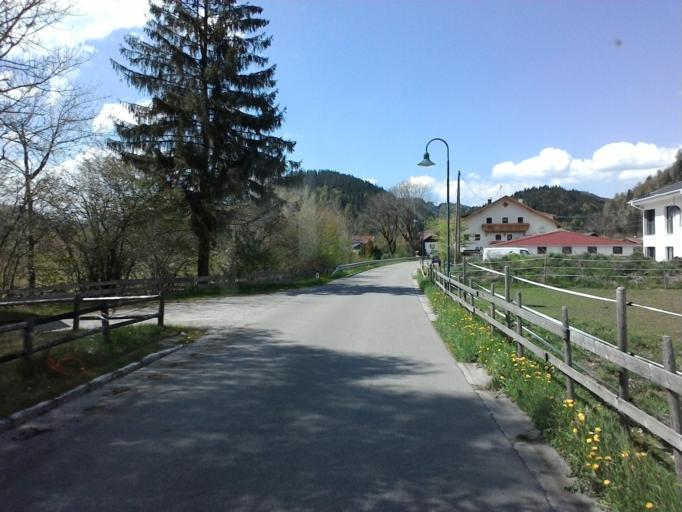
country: AT
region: Tyrol
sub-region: Politischer Bezirk Reutte
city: Musau
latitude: 47.5417
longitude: 10.6772
